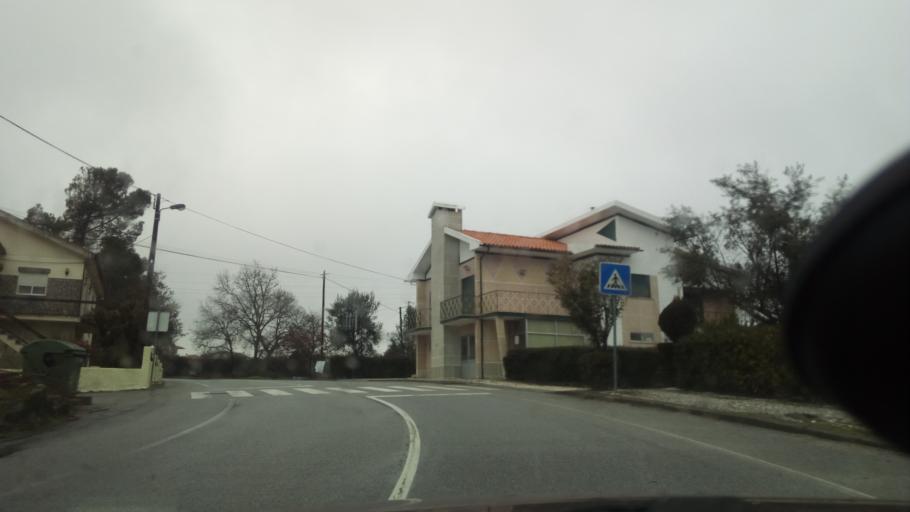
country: PT
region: Viseu
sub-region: Viseu
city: Rio de Loba
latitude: 40.6575
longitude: -7.8730
